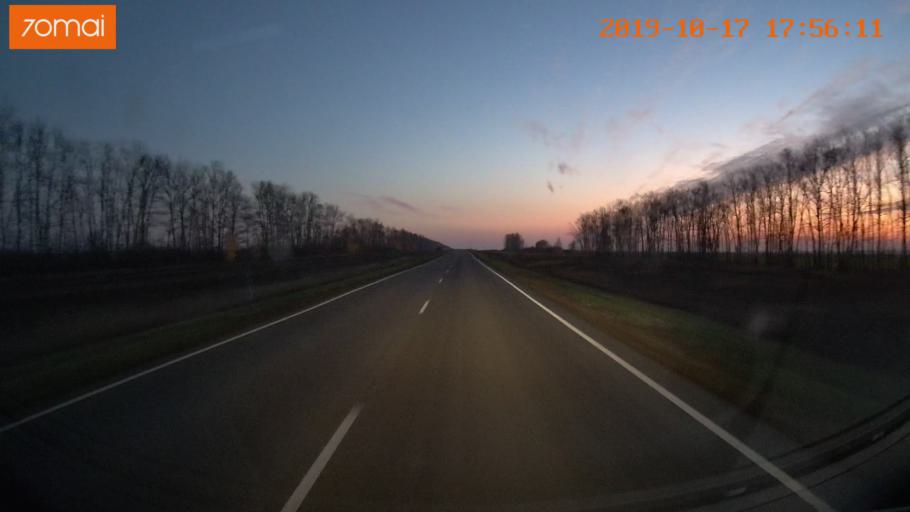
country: RU
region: Tula
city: Kurkino
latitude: 53.5830
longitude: 38.6497
